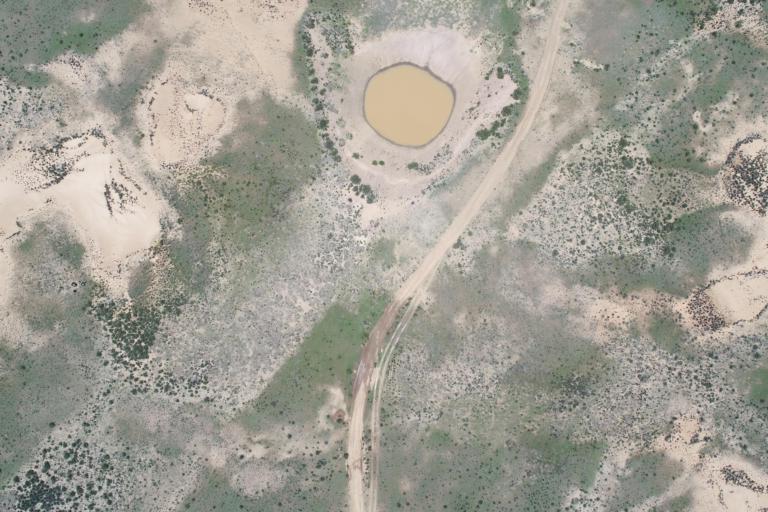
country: BO
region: La Paz
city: Patacamaya
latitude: -17.2824
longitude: -68.5072
